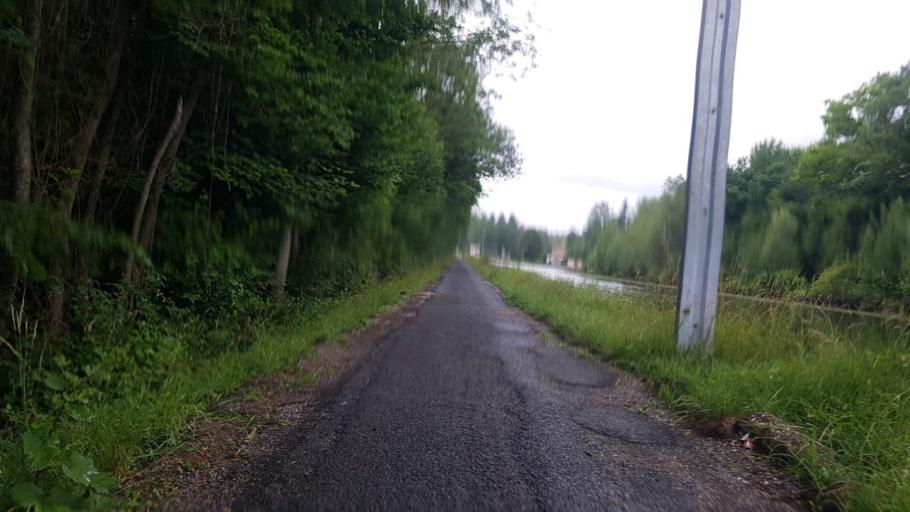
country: FR
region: Champagne-Ardenne
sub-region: Departement de la Marne
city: Vitry-le-Francois
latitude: 48.7474
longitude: 4.5753
